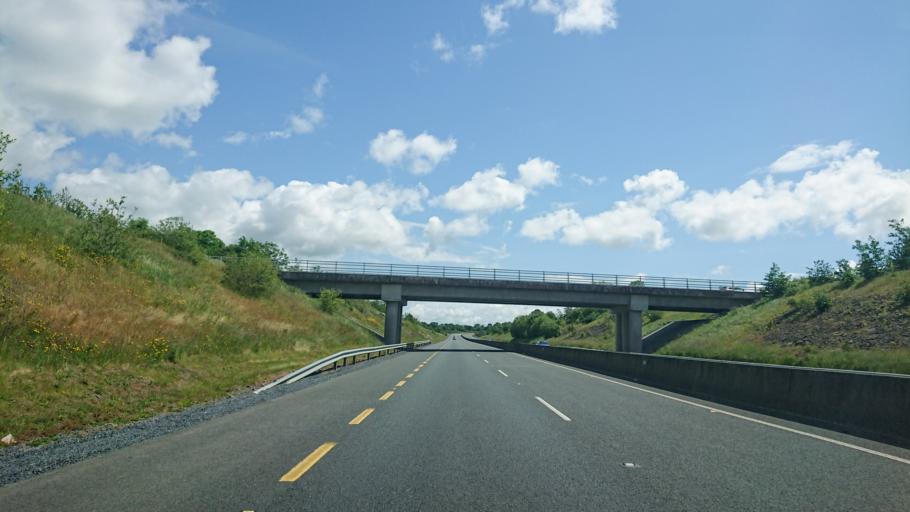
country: IE
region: Munster
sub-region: Waterford
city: Waterford
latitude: 52.2884
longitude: -7.1254
